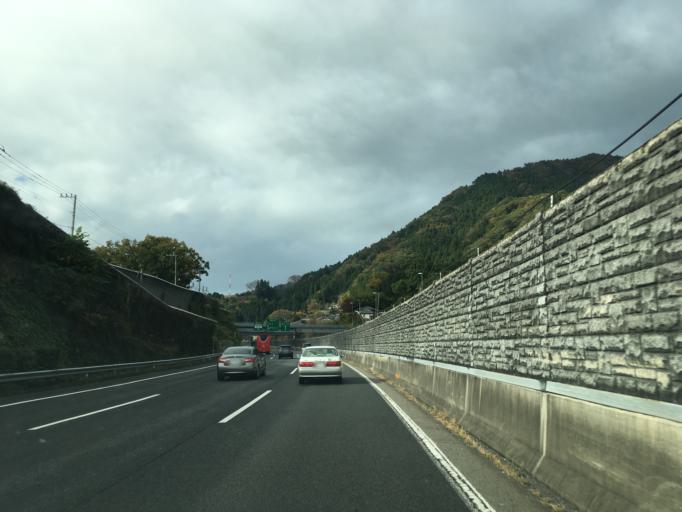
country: JP
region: Yamanashi
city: Uenohara
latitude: 35.6329
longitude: 139.0515
